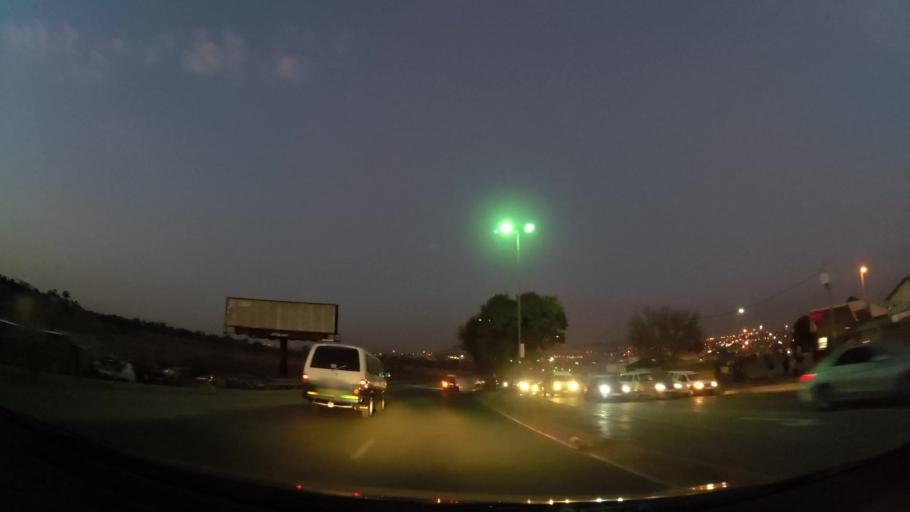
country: ZA
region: Gauteng
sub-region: City of Johannesburg Metropolitan Municipality
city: Roodepoort
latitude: -26.2189
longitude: 27.9194
